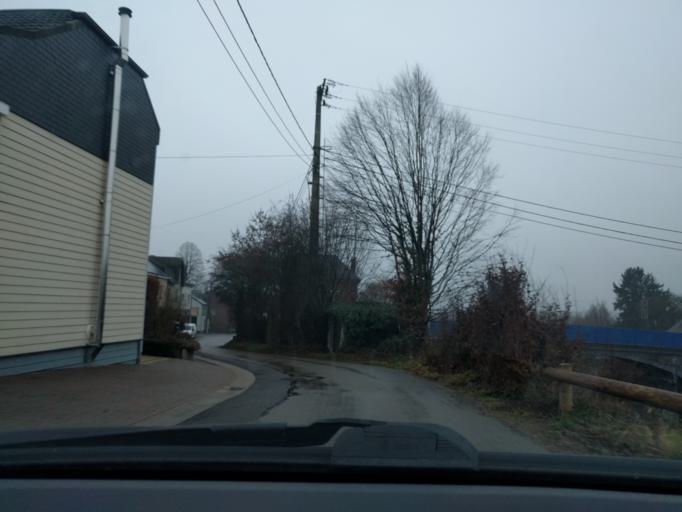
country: BE
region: Wallonia
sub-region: Province du Luxembourg
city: Gouvy
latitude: 50.1921
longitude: 5.9511
